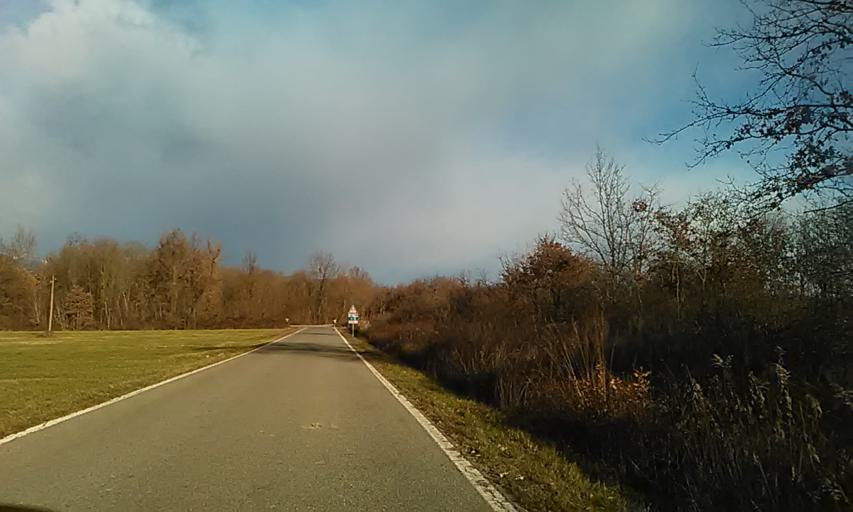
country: IT
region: Piedmont
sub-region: Provincia di Biella
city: Brusnengo
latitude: 45.5700
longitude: 8.2722
